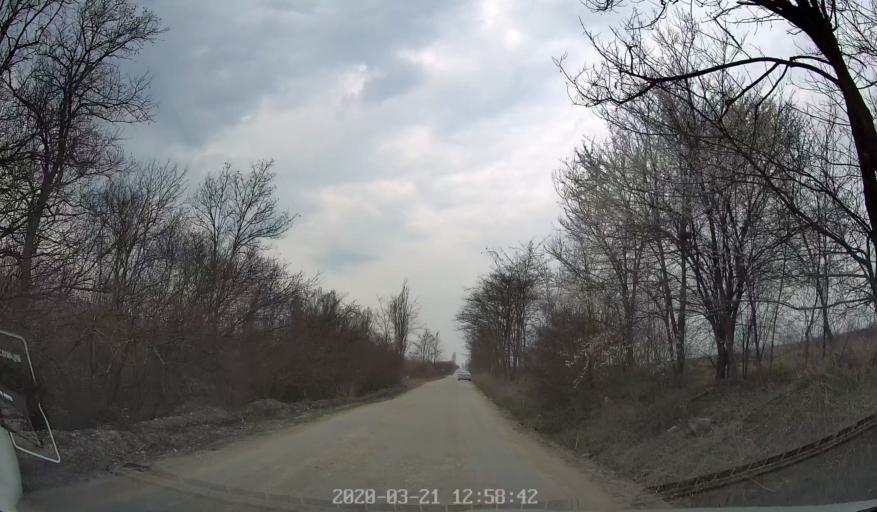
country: MD
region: Laloveni
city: Ialoveni
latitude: 46.9612
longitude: 28.7385
